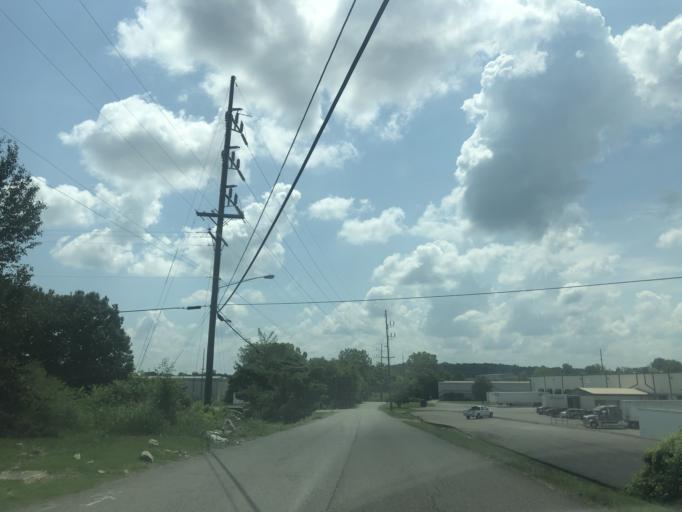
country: US
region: Tennessee
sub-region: Rutherford County
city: La Vergne
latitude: 36.0165
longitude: -86.6028
